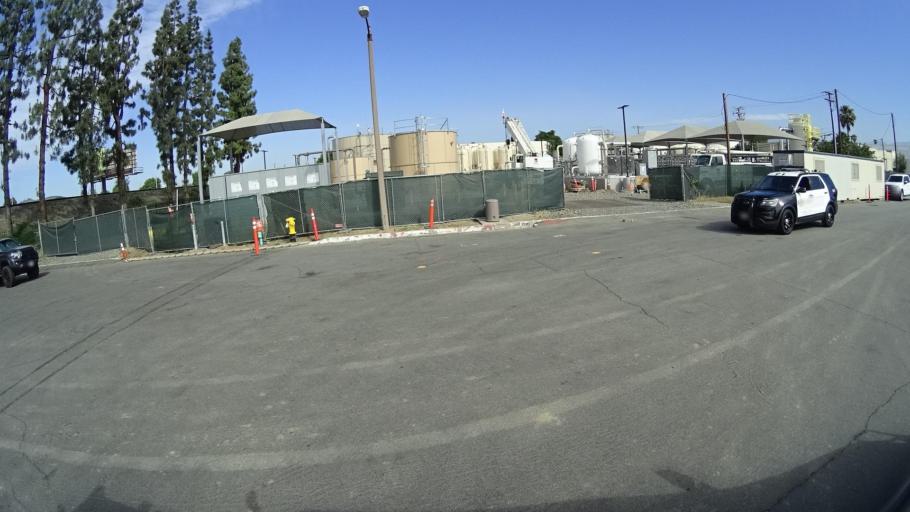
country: US
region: California
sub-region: Los Angeles County
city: La Puente
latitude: 34.0245
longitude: -117.9597
